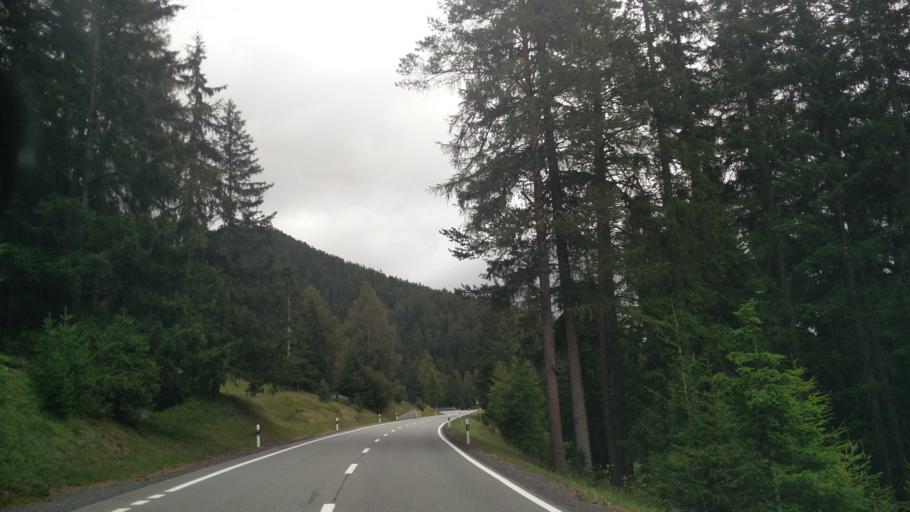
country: CH
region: Grisons
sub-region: Inn District
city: Zernez
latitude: 46.6923
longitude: 10.1301
